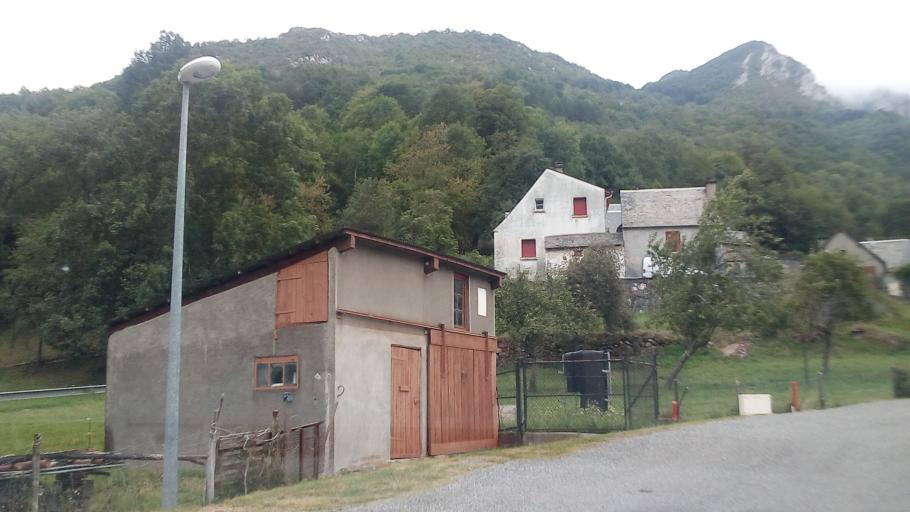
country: FR
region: Midi-Pyrenees
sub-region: Departement des Hautes-Pyrenees
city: La Barthe-de-Neste
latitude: 42.9455
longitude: 0.3747
